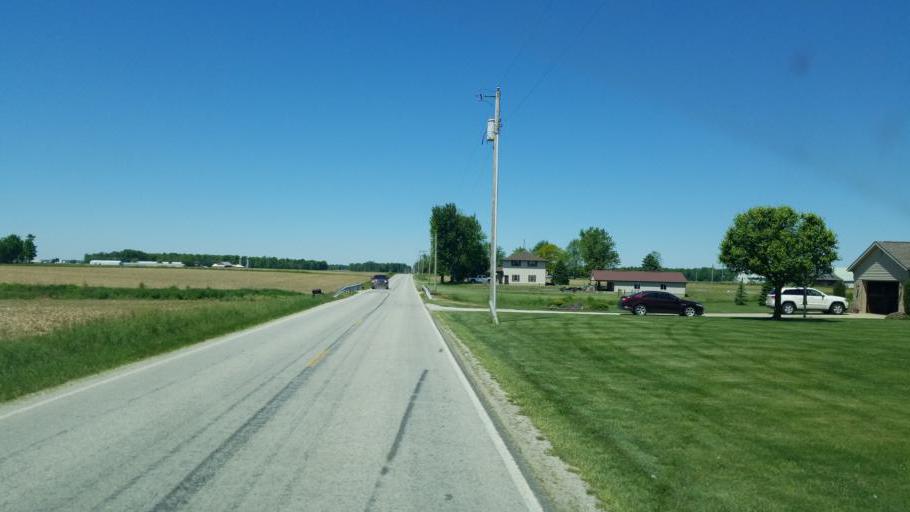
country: US
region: Ohio
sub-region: Shelby County
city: Fort Loramie
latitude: 40.3571
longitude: -84.3097
